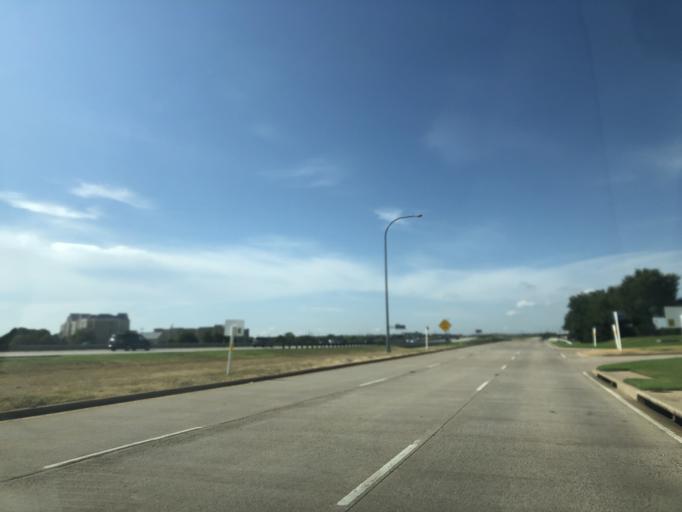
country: US
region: Texas
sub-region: Tarrant County
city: Haslet
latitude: 32.9766
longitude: -97.3086
